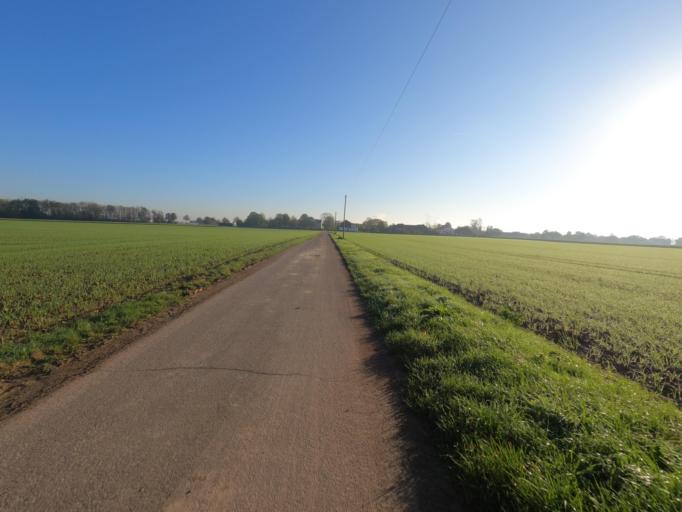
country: DE
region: North Rhine-Westphalia
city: Erkelenz
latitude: 51.0652
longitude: 6.3211
